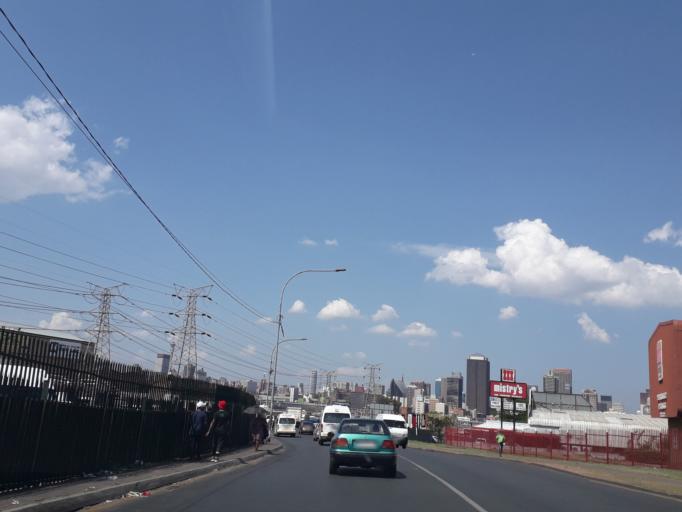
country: ZA
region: Gauteng
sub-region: City of Johannesburg Metropolitan Municipality
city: Johannesburg
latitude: -26.2108
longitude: 28.0200
